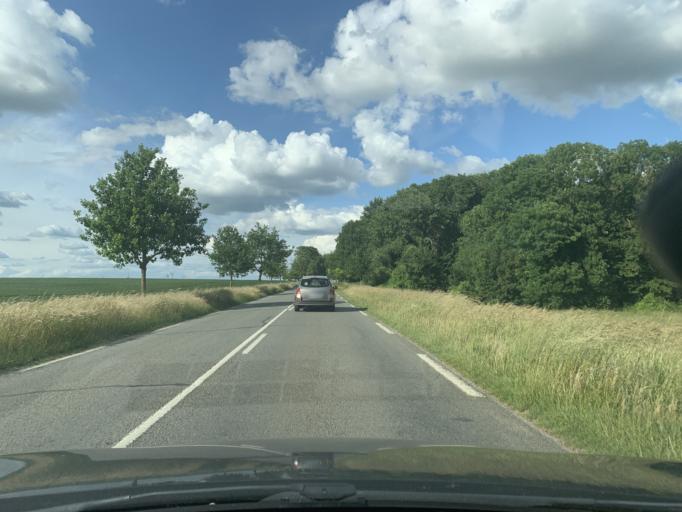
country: FR
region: Picardie
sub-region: Departement de la Somme
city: Moislains
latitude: 49.9729
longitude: 2.9914
